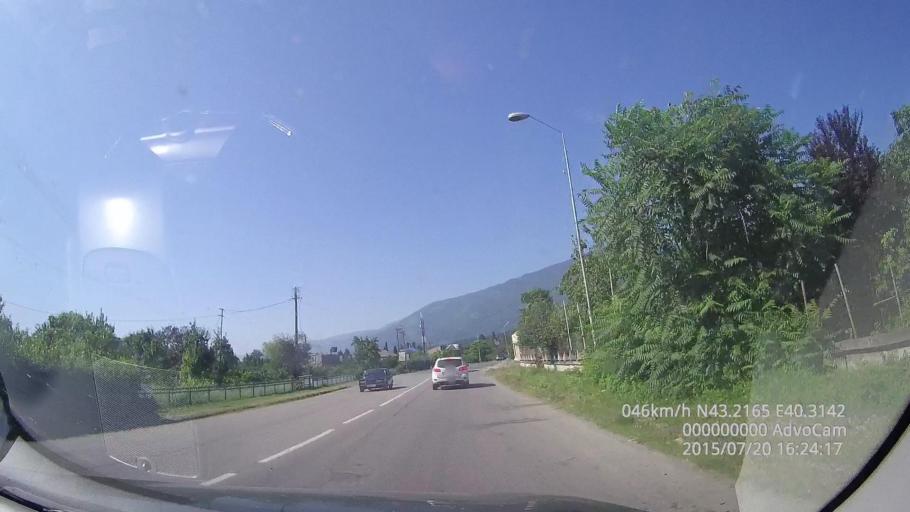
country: GE
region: Abkhazia
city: Bich'vinta
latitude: 43.2165
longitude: 40.3142
